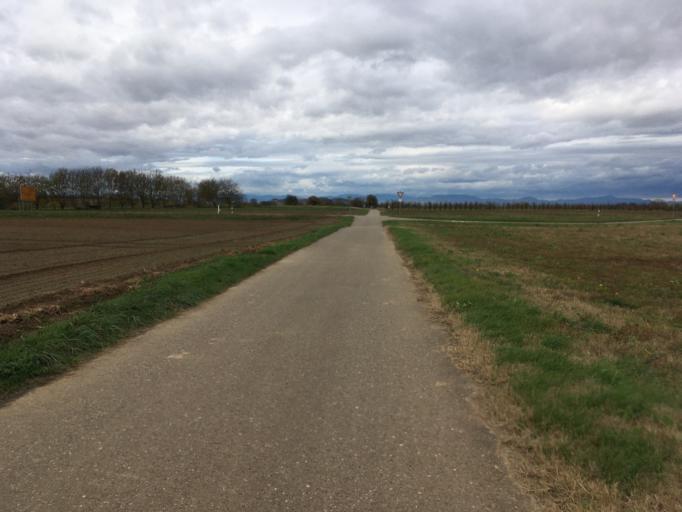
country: DE
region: Baden-Wuerttemberg
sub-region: Freiburg Region
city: Endingen
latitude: 48.1471
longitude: 7.6839
